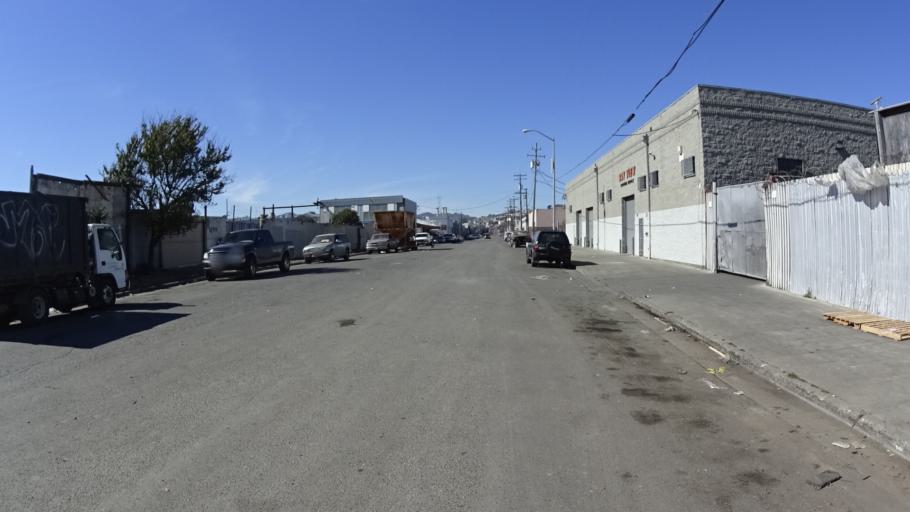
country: US
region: California
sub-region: San Mateo County
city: Brisbane
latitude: 37.7252
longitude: -122.3853
